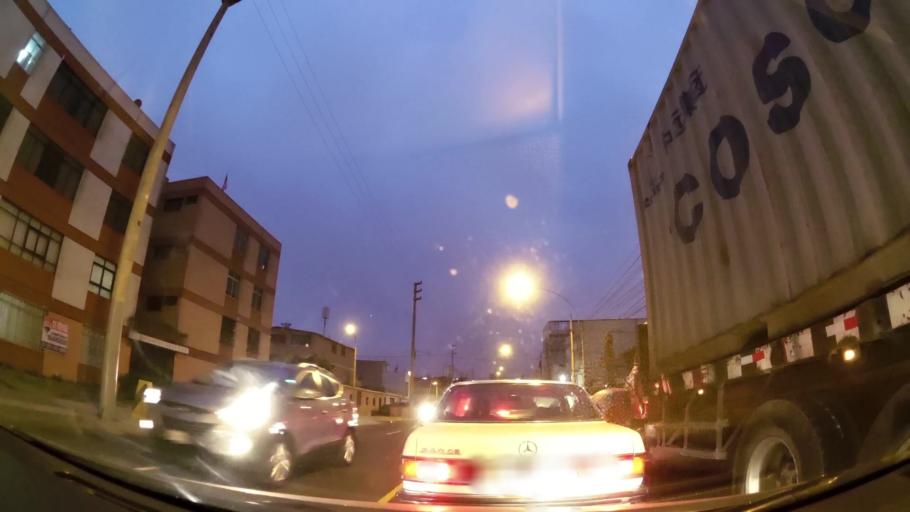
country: PE
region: Callao
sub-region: Callao
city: Callao
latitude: -12.0798
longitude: -77.0944
